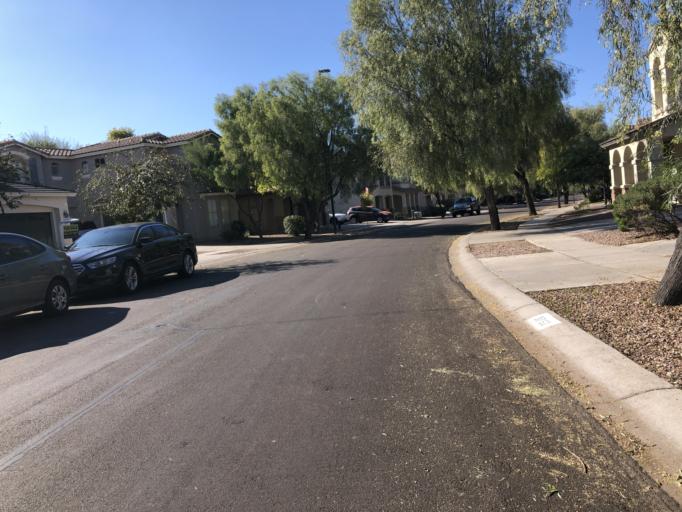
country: US
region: Arizona
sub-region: Maricopa County
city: Queen Creek
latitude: 33.2730
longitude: -111.7086
